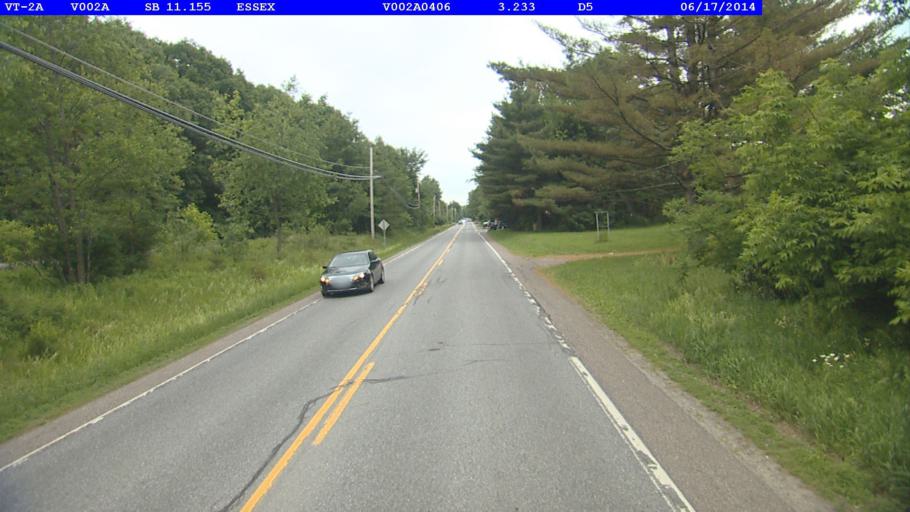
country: US
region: Vermont
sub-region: Chittenden County
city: Colchester
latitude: 44.5256
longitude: -73.1255
